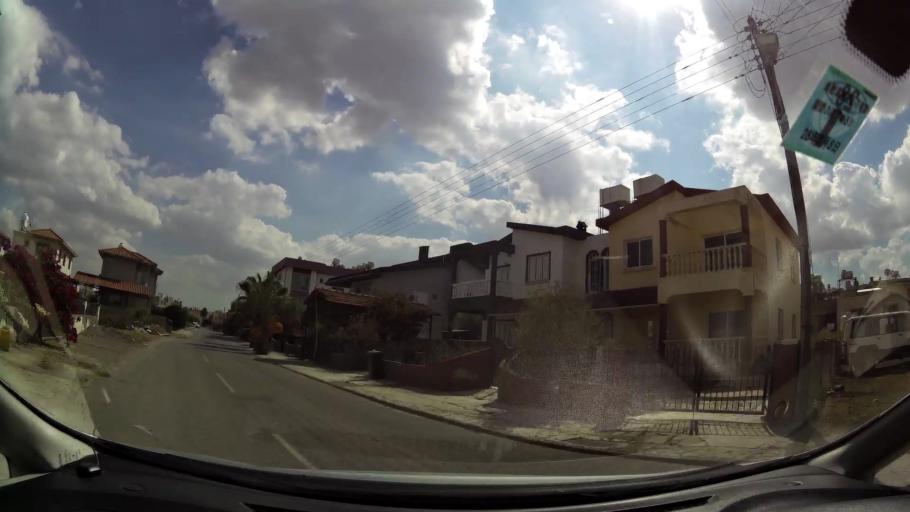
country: CY
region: Lefkosia
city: Nicosia
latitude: 35.2182
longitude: 33.2952
